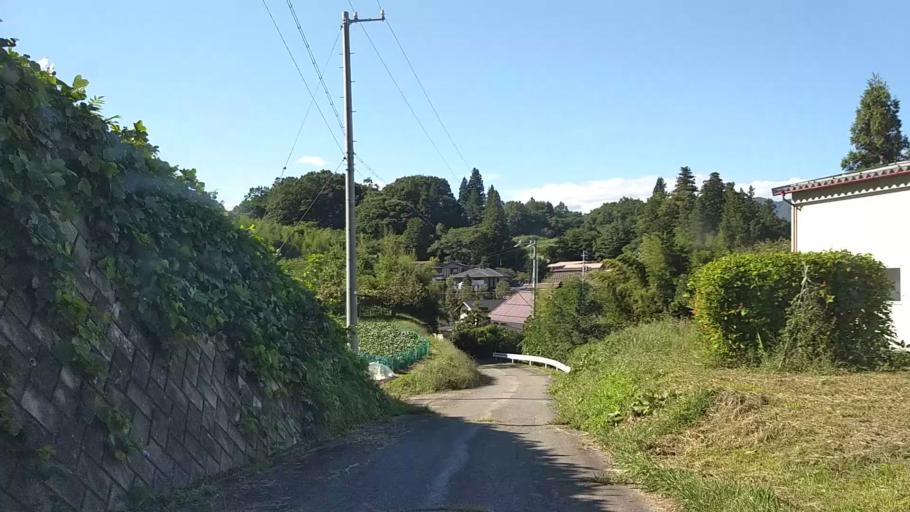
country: JP
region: Nagano
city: Nagano-shi
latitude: 36.5959
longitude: 138.0855
